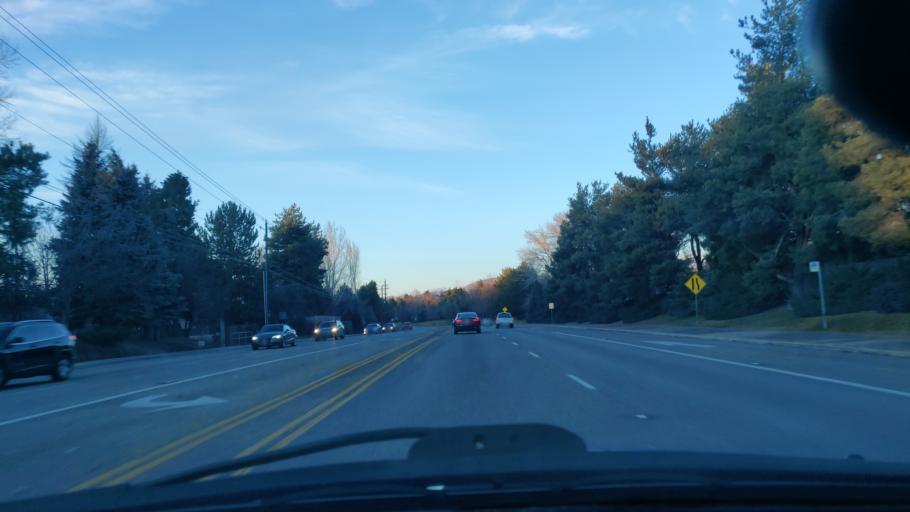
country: US
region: Idaho
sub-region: Ada County
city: Boise
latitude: 43.5862
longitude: -116.1734
